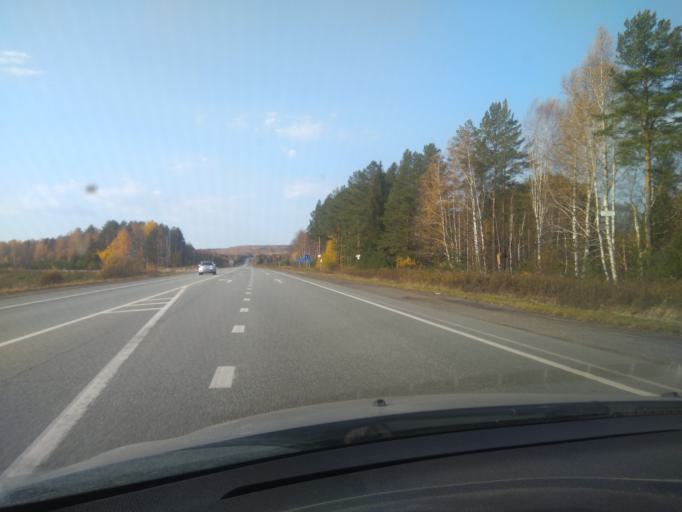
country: RU
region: Sverdlovsk
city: Atig
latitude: 56.7344
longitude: 59.4335
